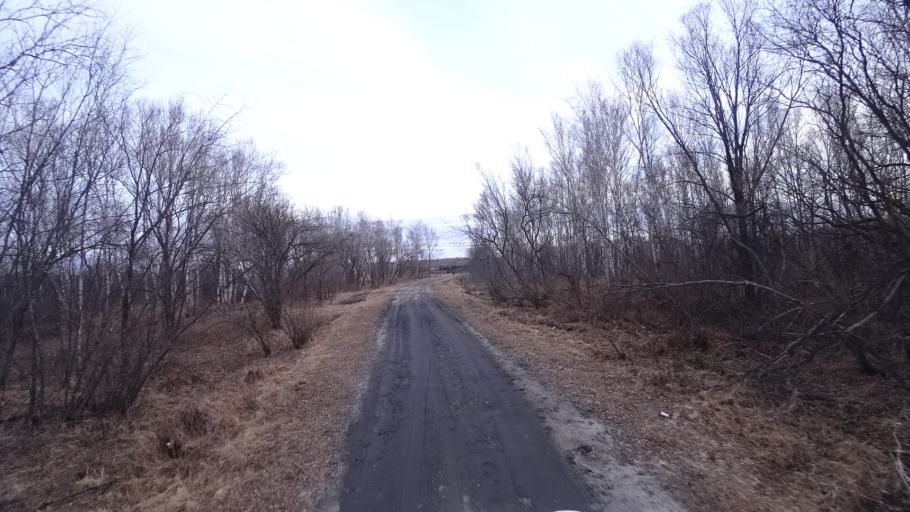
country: RU
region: Amur
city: Bureya
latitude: 50.0189
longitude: 129.7808
